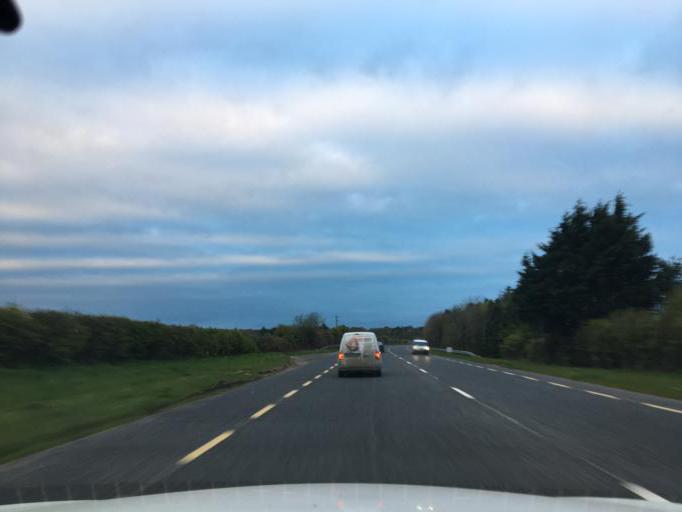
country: IE
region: Leinster
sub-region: Loch Garman
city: Loch Garman
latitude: 52.3034
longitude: -6.4657
